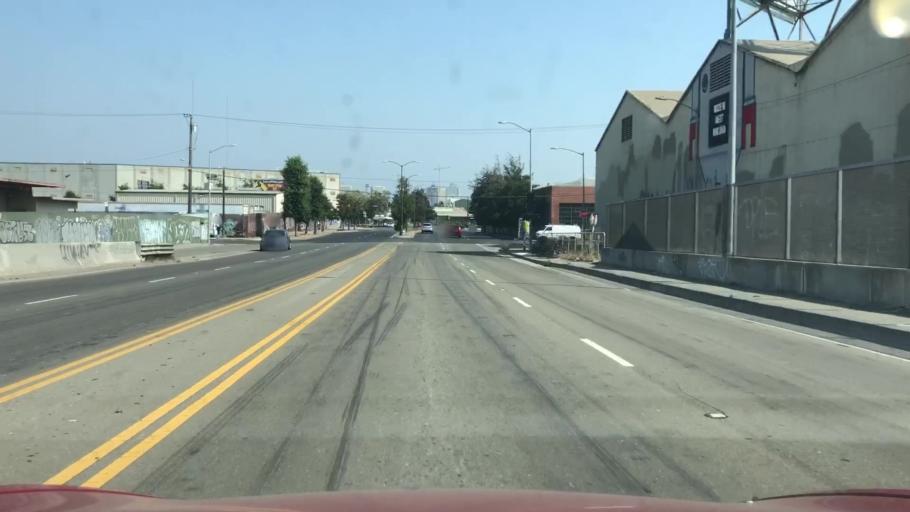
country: US
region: California
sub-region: Alameda County
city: Emeryville
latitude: 37.8179
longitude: -122.2917
